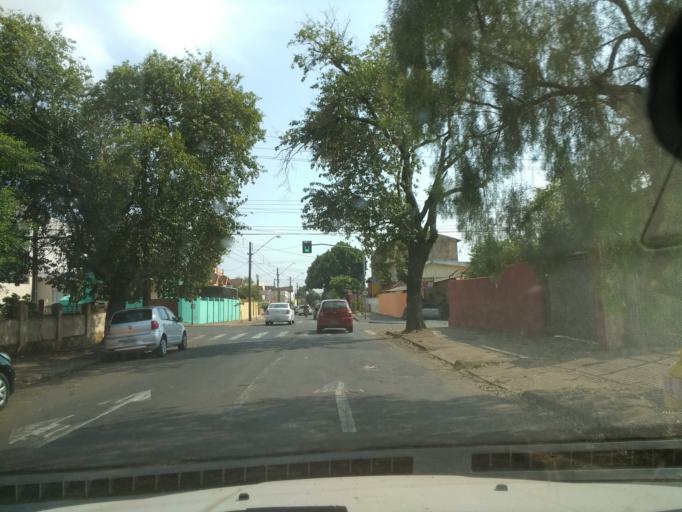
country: BR
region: Parana
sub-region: Londrina
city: Londrina
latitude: -23.3037
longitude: -51.1615
